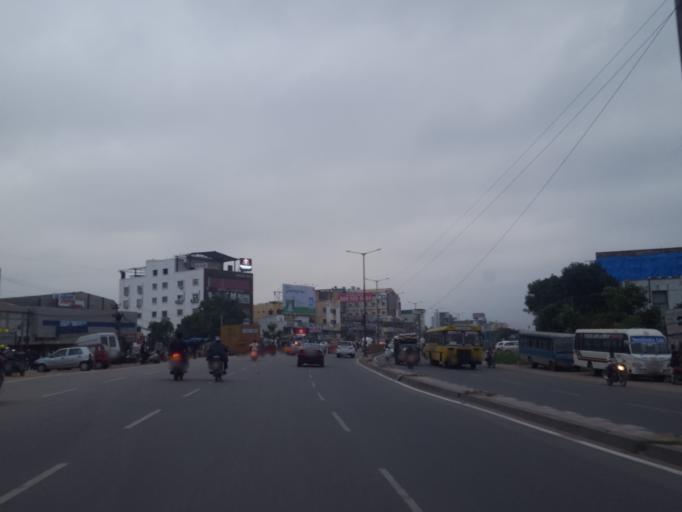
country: IN
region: Telangana
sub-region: Medak
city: Serilingampalle
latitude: 17.5032
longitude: 78.3109
